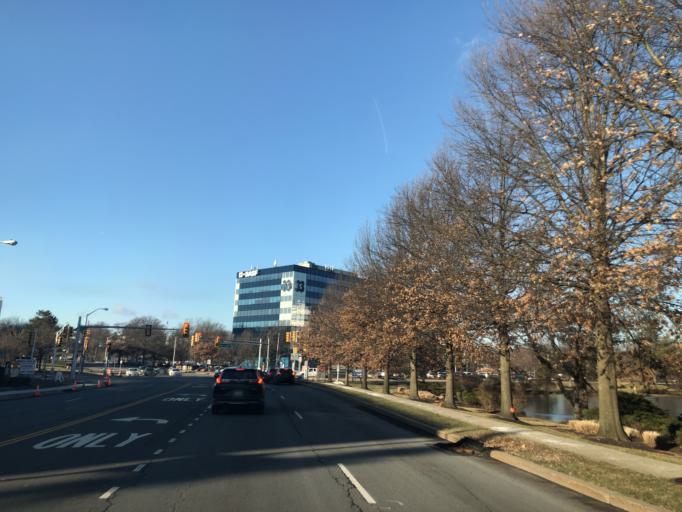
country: US
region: New Jersey
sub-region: Middlesex County
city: Iselin
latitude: 40.5632
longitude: -74.3284
